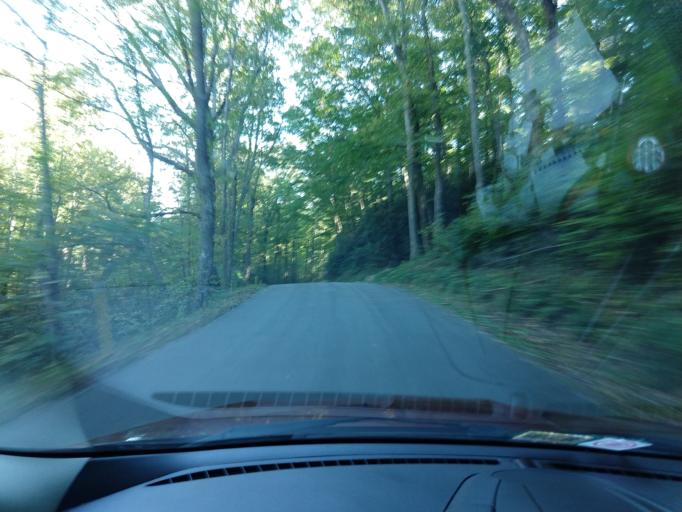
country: US
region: Virginia
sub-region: Alleghany County
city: Clifton Forge
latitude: 37.8531
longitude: -79.8570
